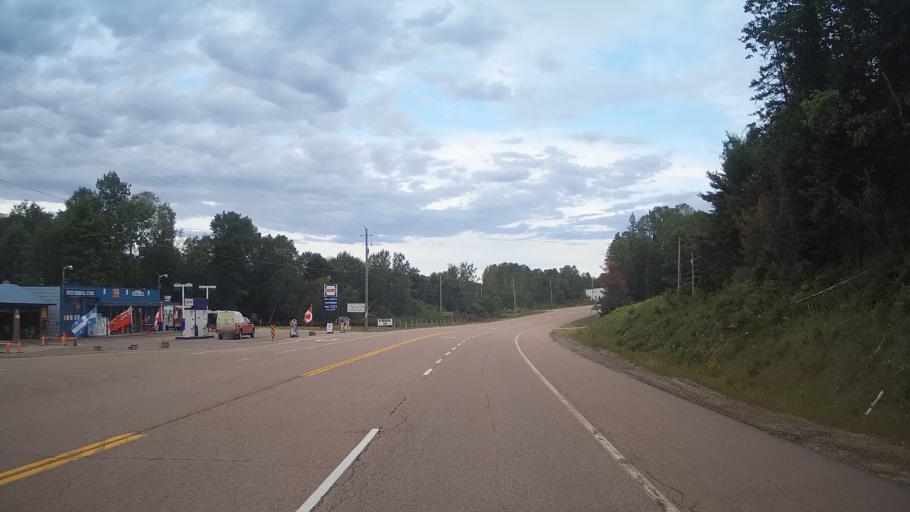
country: CA
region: Ontario
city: Deep River
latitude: 46.2132
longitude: -77.8977
